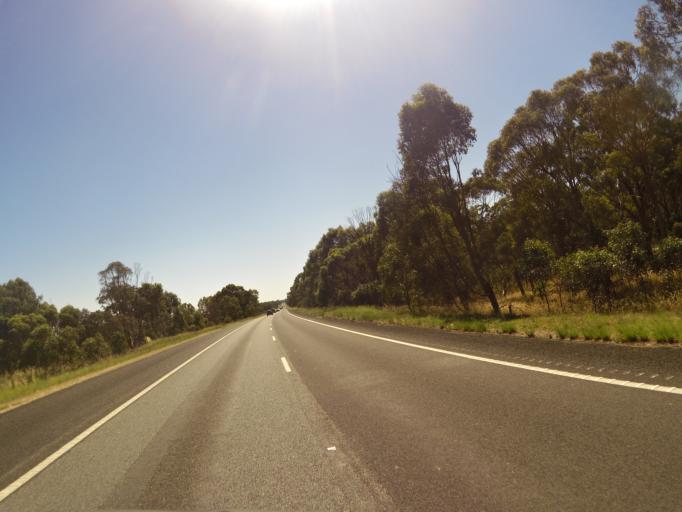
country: AU
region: Victoria
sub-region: Greater Shepparton
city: Shepparton
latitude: -36.8787
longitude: 145.2715
